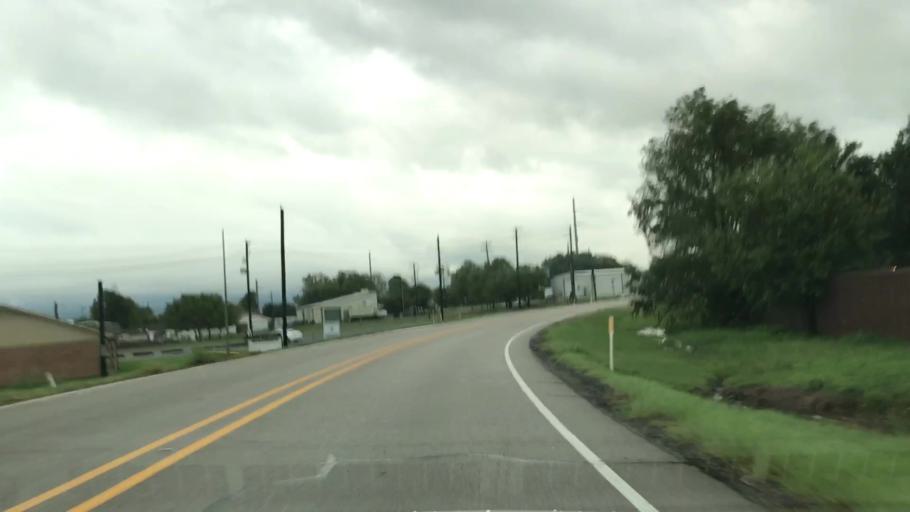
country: US
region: Texas
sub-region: Collin County
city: Wylie
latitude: 33.0275
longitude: -96.5400
